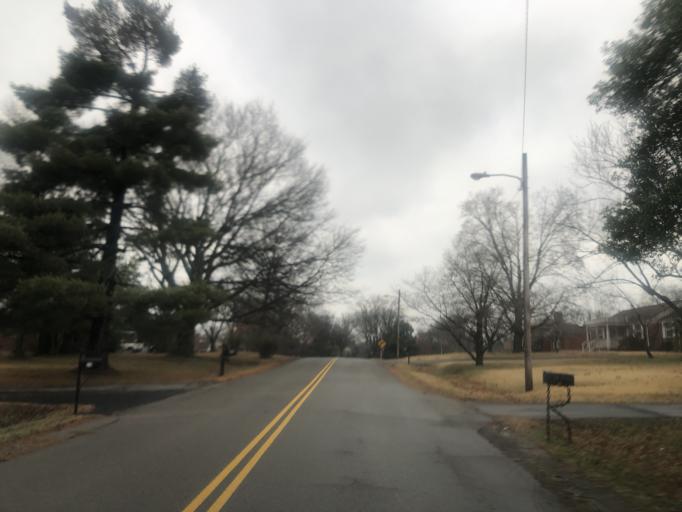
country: US
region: Tennessee
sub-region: Davidson County
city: Lakewood
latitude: 36.1721
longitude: -86.6922
